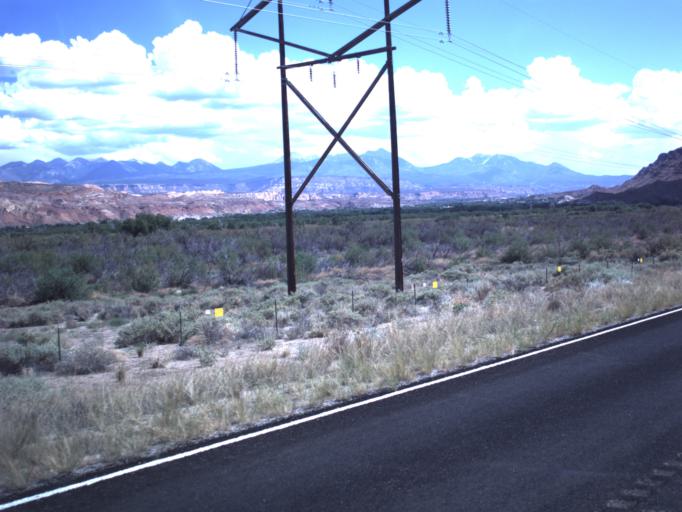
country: US
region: Utah
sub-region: Grand County
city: Moab
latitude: 38.5908
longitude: -109.5946
